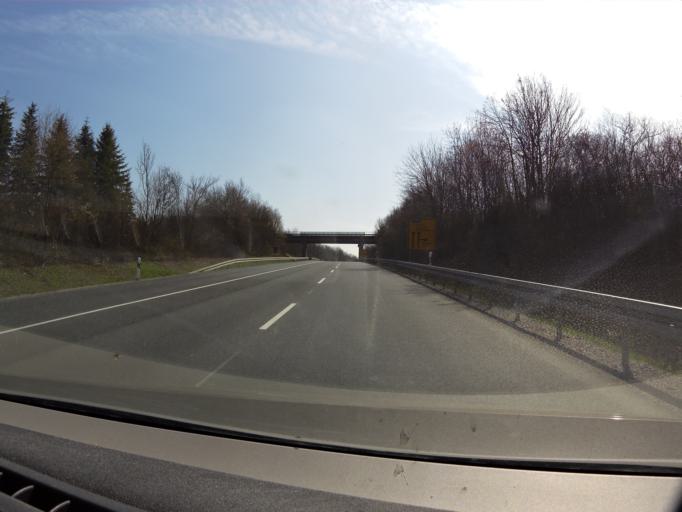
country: DE
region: Bavaria
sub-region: Regierungsbezirk Unterfranken
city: Ochsenfurt
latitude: 49.6535
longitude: 10.0744
